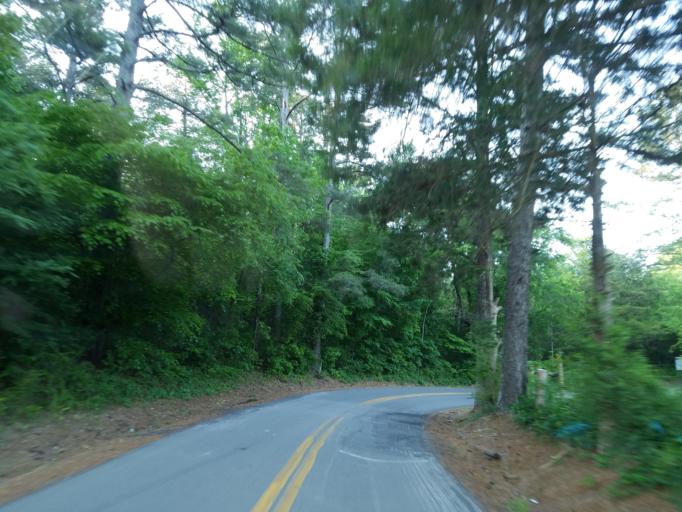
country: US
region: Georgia
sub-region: Gordon County
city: Calhoun
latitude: 34.5247
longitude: -85.1197
